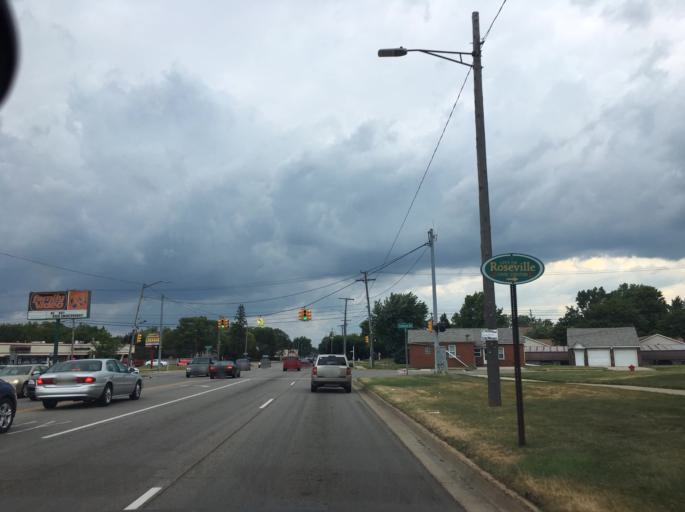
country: US
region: Michigan
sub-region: Macomb County
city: Roseville
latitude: 42.5164
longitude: -82.9398
